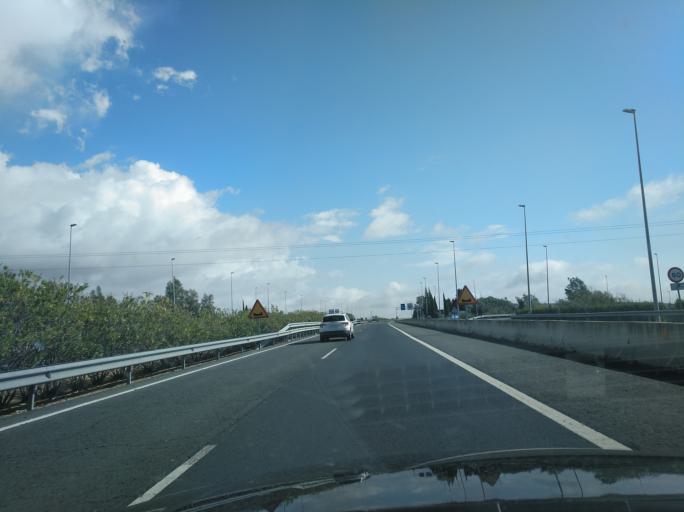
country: ES
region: Andalusia
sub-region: Provincia de Huelva
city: Gibraleon
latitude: 37.3562
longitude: -6.9607
